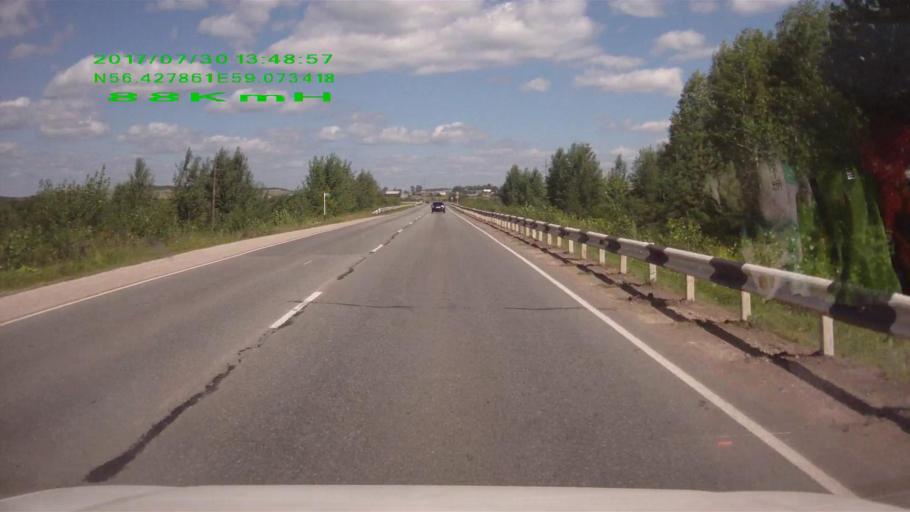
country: RU
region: Sverdlovsk
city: Mikhaylovsk
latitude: 56.4282
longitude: 59.0743
